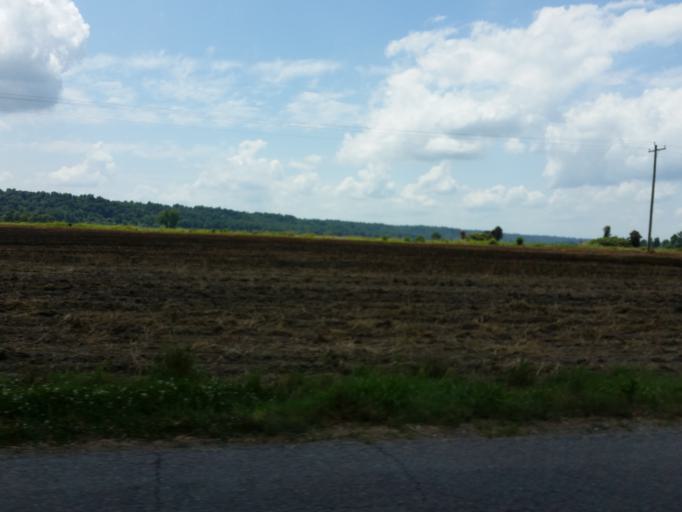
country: US
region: Kentucky
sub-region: Fulton County
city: Hickman
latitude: 36.5489
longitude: -89.2425
